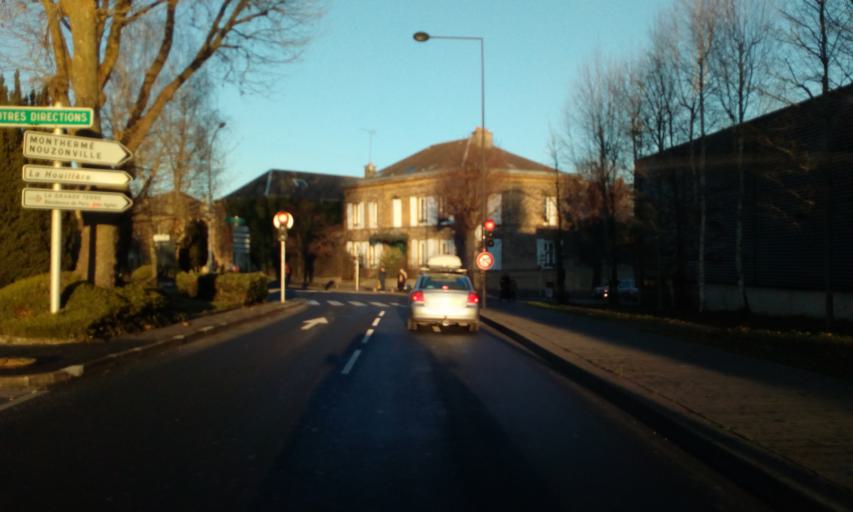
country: FR
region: Champagne-Ardenne
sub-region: Departement des Ardennes
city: Charleville-Mezieres
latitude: 49.7745
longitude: 4.7152
